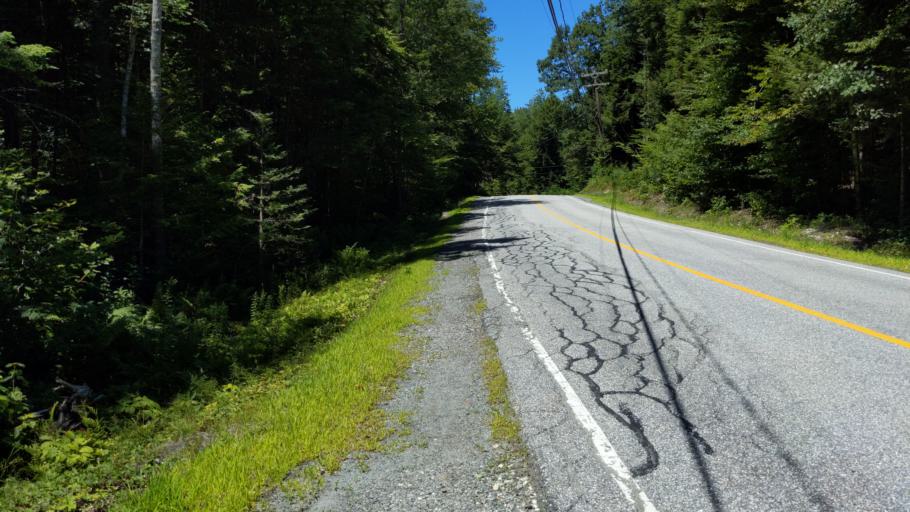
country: US
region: New Hampshire
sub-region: Sullivan County
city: Grantham
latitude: 43.5145
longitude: -72.1091
